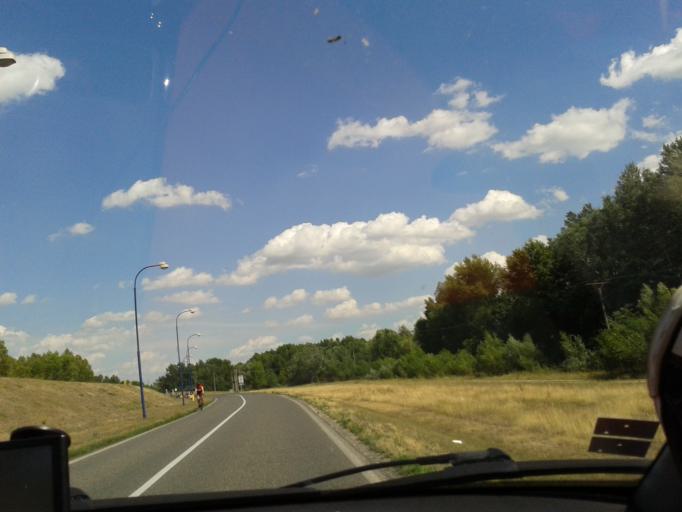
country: HU
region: Gyor-Moson-Sopron
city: Rajka
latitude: 48.0251
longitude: 17.2114
